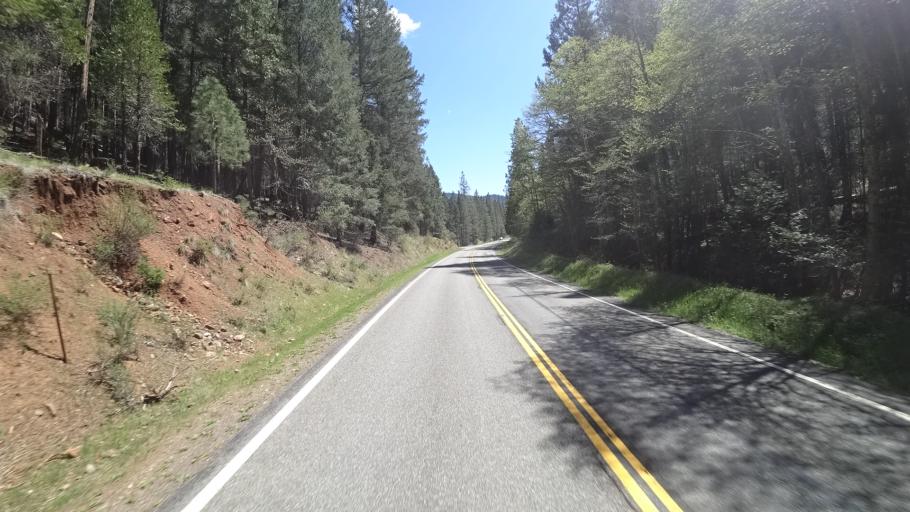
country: US
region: California
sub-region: Trinity County
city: Weaverville
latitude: 40.7630
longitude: -122.8877
